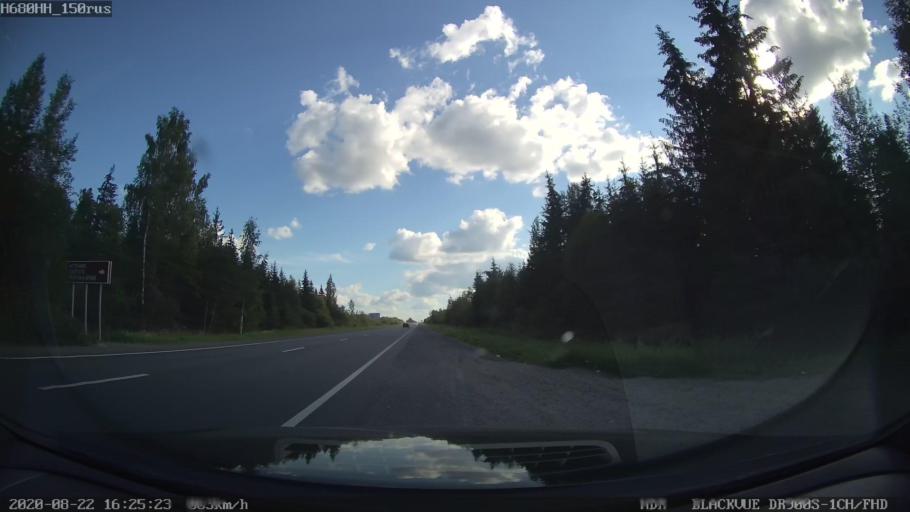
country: RU
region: Tverskaya
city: Rameshki
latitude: 57.3227
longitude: 36.0906
